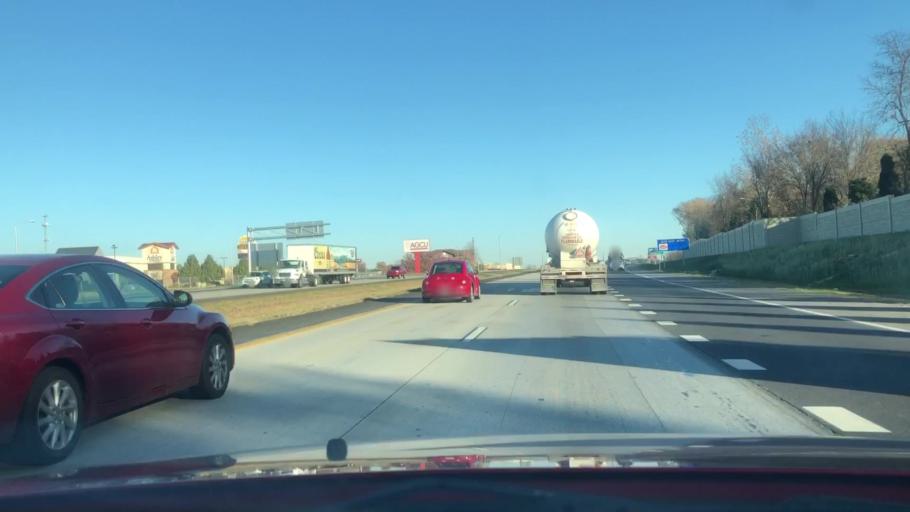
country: US
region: Missouri
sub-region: Greene County
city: Springfield
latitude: 37.1418
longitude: -93.2670
